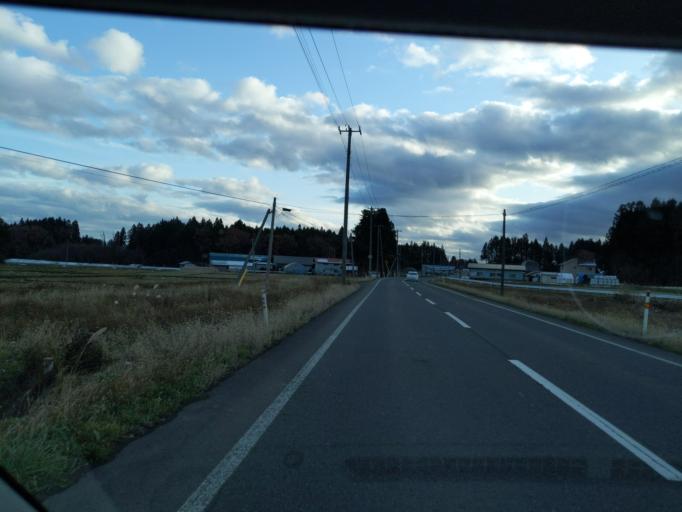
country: JP
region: Iwate
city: Mizusawa
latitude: 39.1121
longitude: 141.0530
